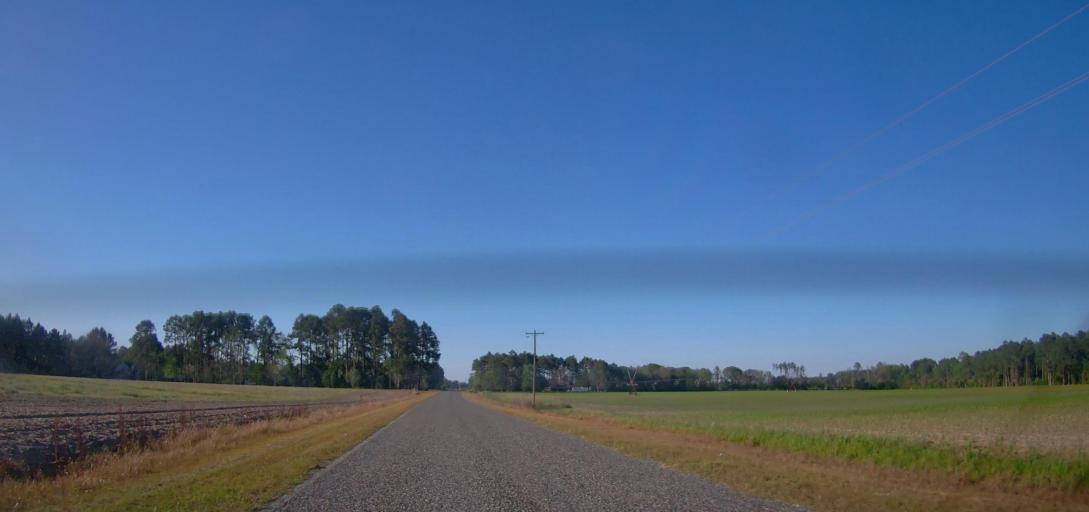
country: US
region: Georgia
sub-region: Ben Hill County
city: Fitzgerald
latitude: 31.6665
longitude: -83.1468
